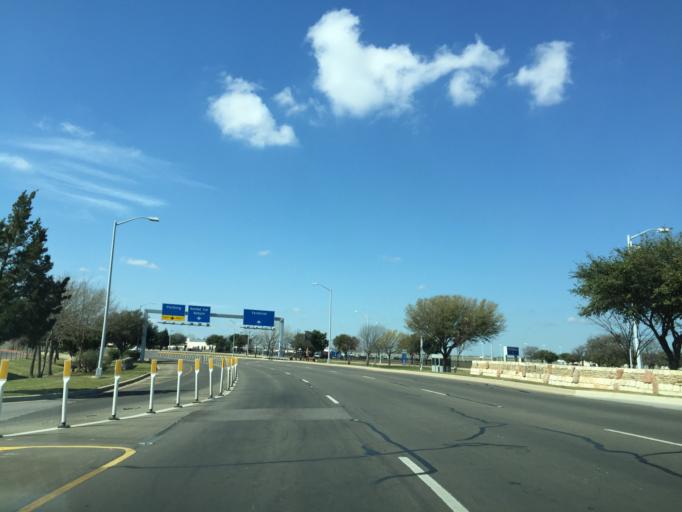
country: US
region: Texas
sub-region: Travis County
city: Hornsby Bend
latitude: 30.2102
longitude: -97.6674
